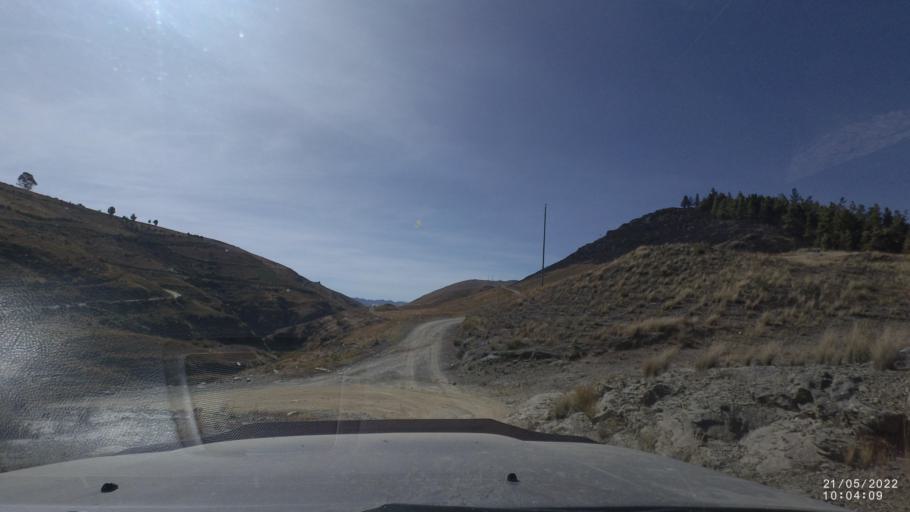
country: BO
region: Cochabamba
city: Colomi
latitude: -17.3395
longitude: -65.9885
